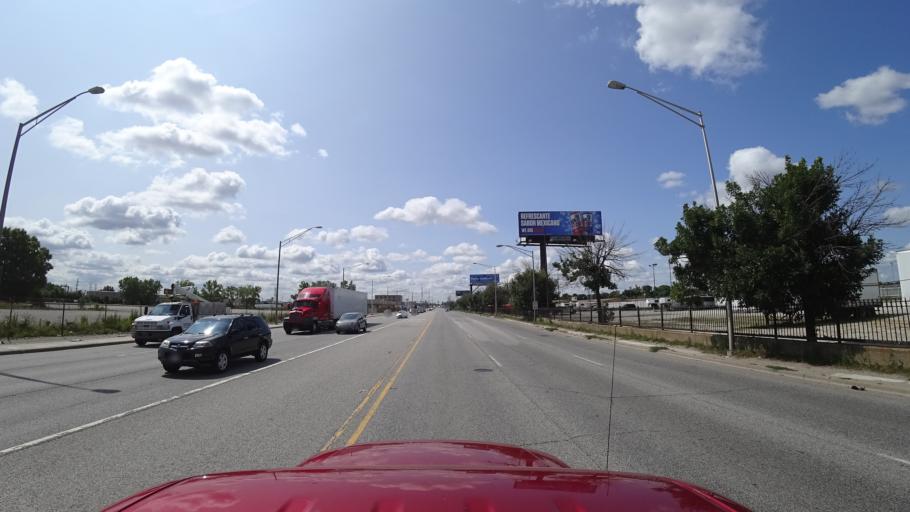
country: US
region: Illinois
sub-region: Cook County
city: Cicero
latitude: 41.8286
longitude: -87.7437
